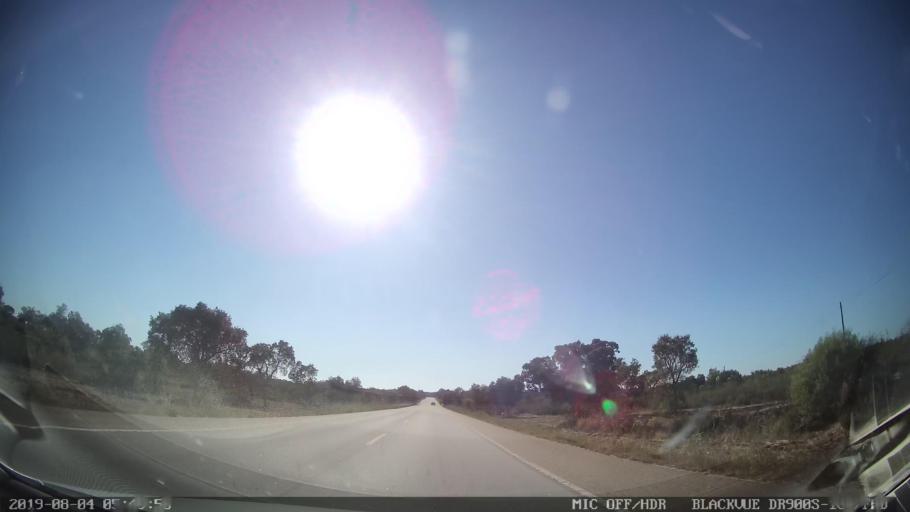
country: PT
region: Portalegre
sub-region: Gaviao
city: Gaviao
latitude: 39.4407
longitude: -7.8596
